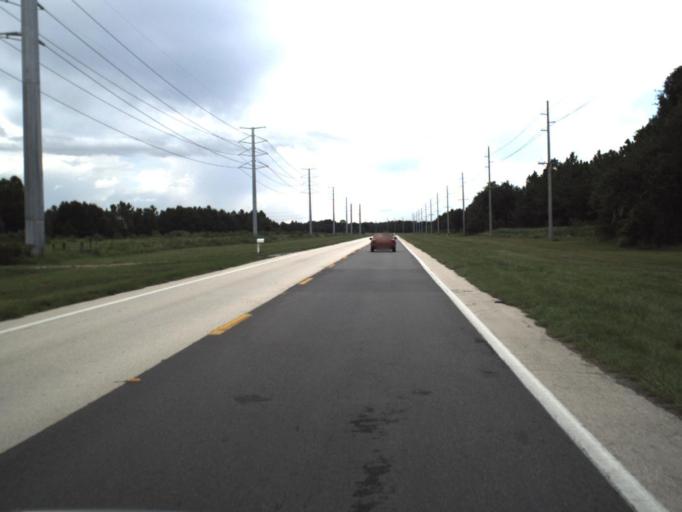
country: US
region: Florida
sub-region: Polk County
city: Mulberry
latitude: 27.7767
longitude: -81.9876
